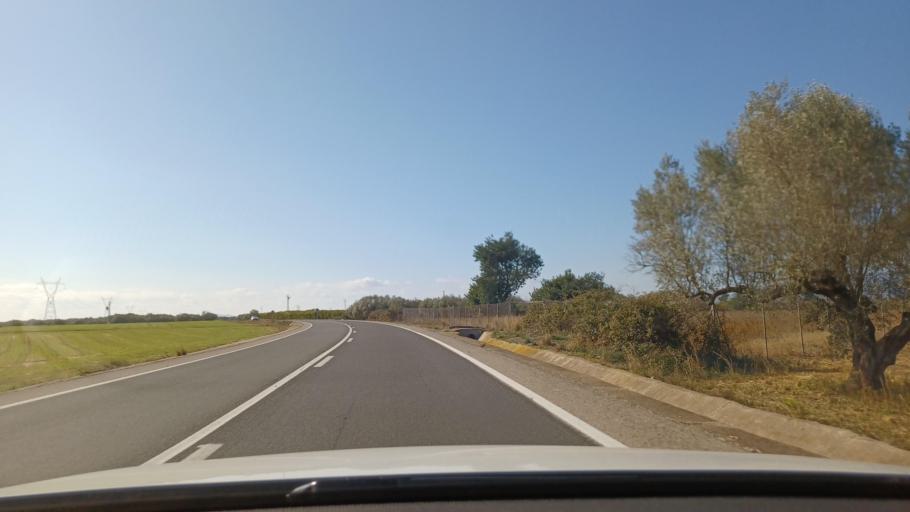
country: ES
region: Catalonia
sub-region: Provincia de Tarragona
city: Santa Barbara
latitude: 40.6736
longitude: 0.4448
